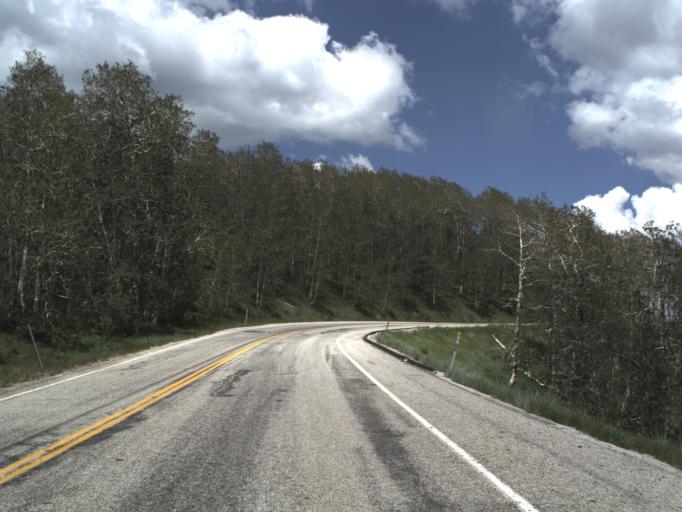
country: US
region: Utah
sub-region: Weber County
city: Wolf Creek
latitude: 41.4062
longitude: -111.5284
